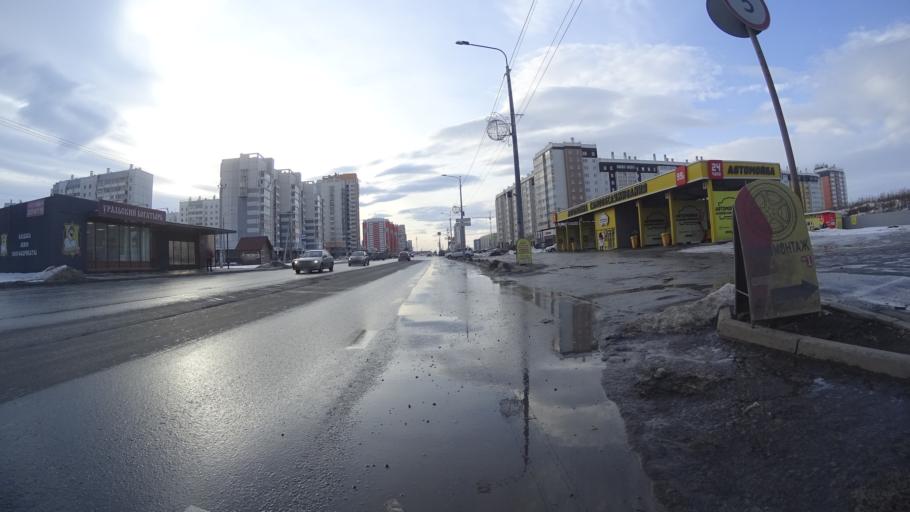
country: RU
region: Chelyabinsk
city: Roshchino
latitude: 55.2094
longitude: 61.2927
